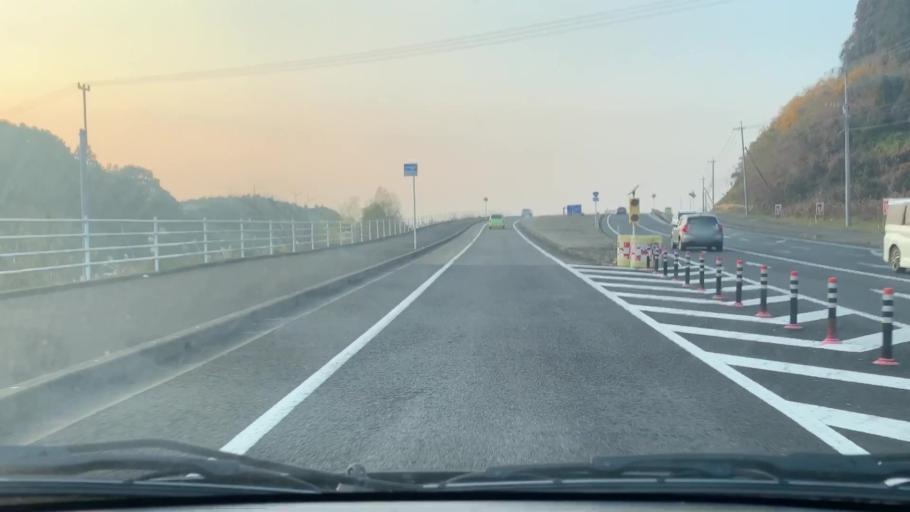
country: JP
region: Saga Prefecture
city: Imaricho-ko
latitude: 33.2627
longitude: 129.9104
